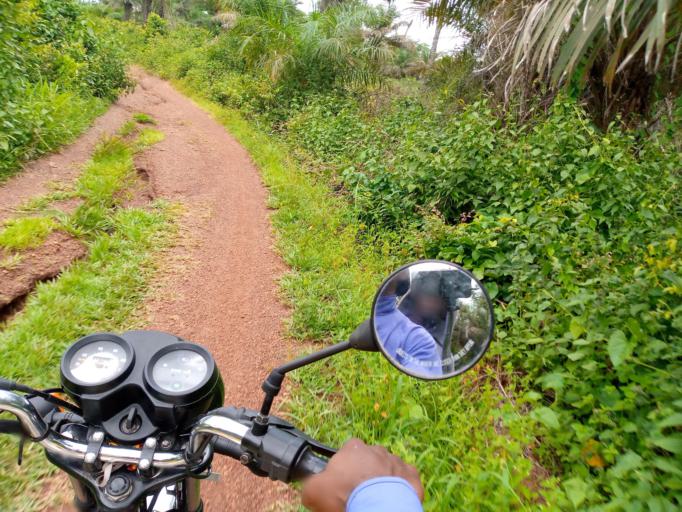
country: SL
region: Northern Province
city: Mange
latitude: 8.9890
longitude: -12.7697
